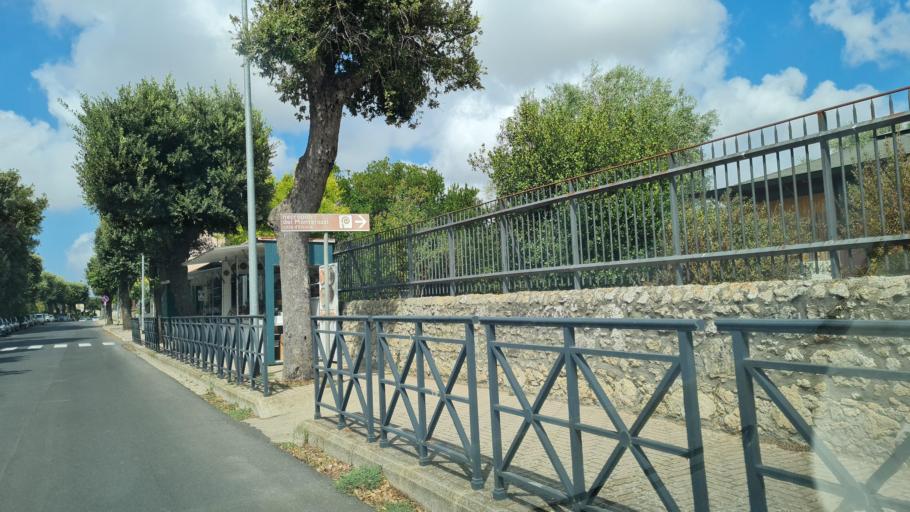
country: IT
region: Latium
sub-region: Provincia di Viterbo
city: Tarquinia
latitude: 42.2496
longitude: 11.7682
